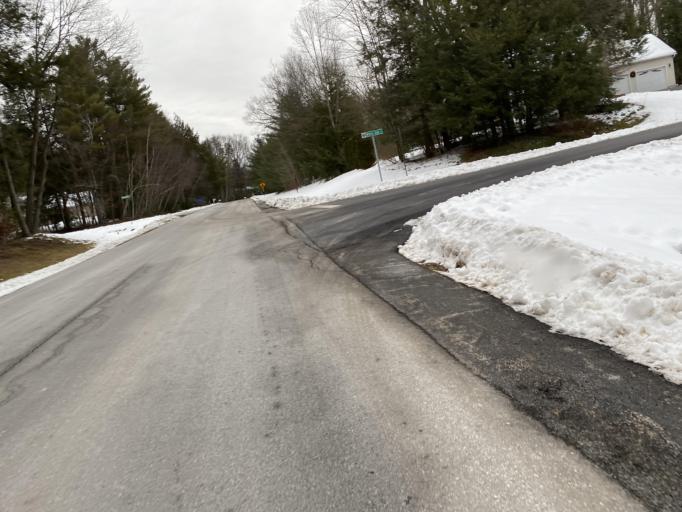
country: US
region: New York
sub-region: Saratoga County
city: Milton
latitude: 43.0952
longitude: -73.9052
